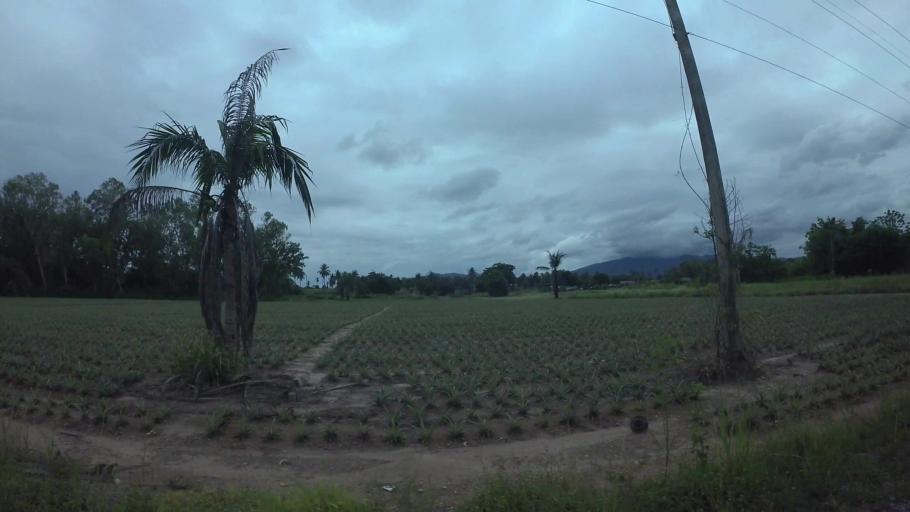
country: TH
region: Chon Buri
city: Si Racha
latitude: 13.1969
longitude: 100.9944
